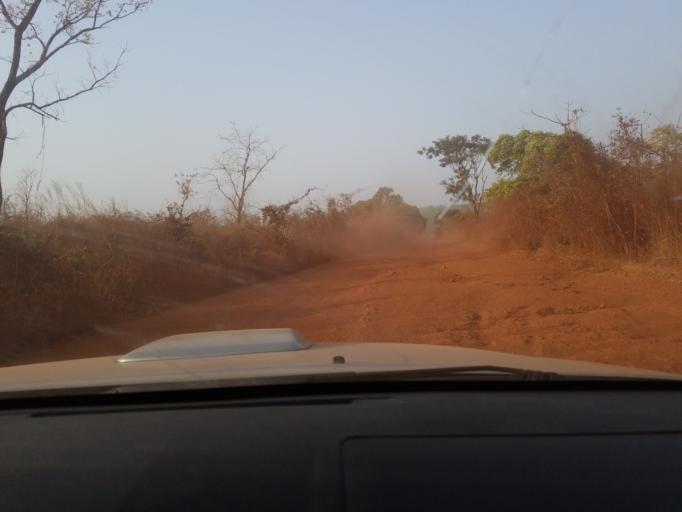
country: GN
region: Boke
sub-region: Gaoual Prefecture
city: Gaoual
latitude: 11.5068
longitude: -13.8595
